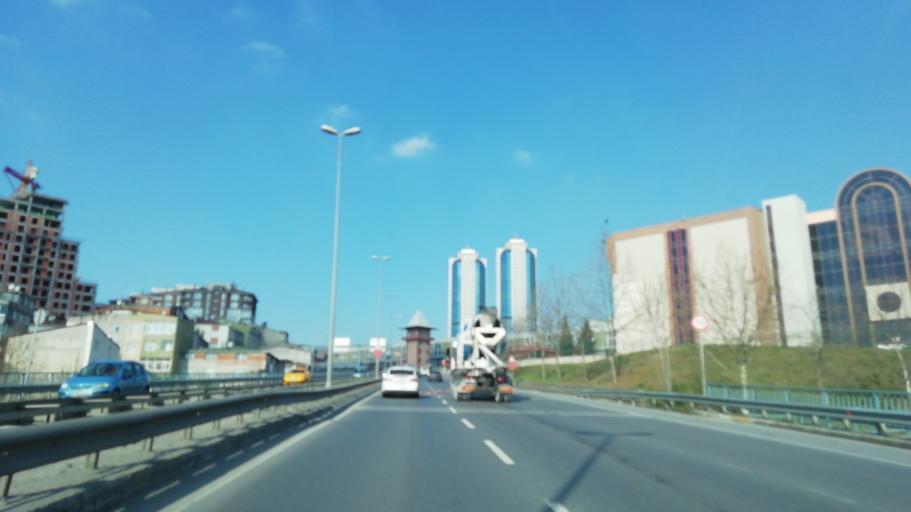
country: TR
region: Istanbul
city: Esenler
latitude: 41.0630
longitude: 28.8681
